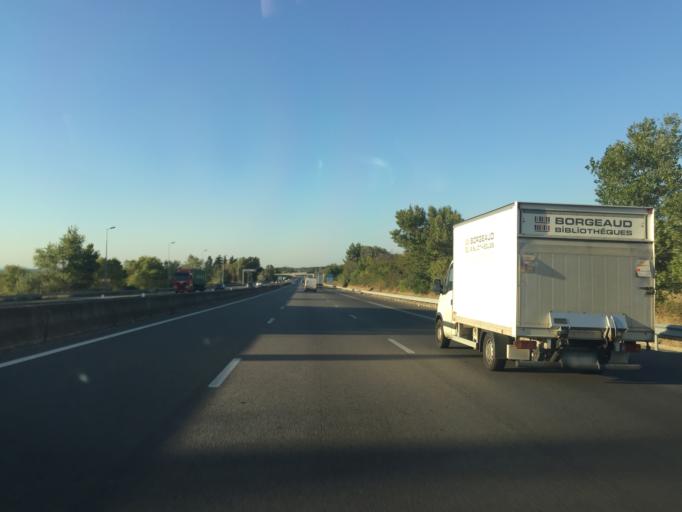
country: FR
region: Provence-Alpes-Cote d'Azur
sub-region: Departement du Vaucluse
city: Morieres-les-Avignon
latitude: 43.9254
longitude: 4.9134
